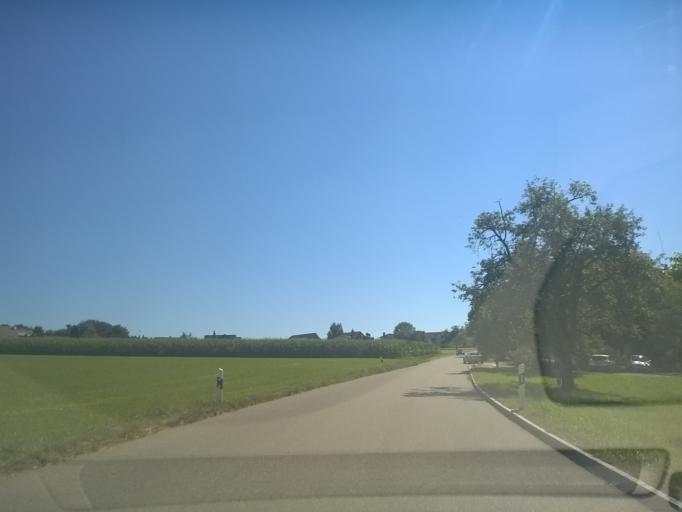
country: CH
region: Zurich
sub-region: Bezirk Winterthur
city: Brutten
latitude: 47.4716
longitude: 8.6668
